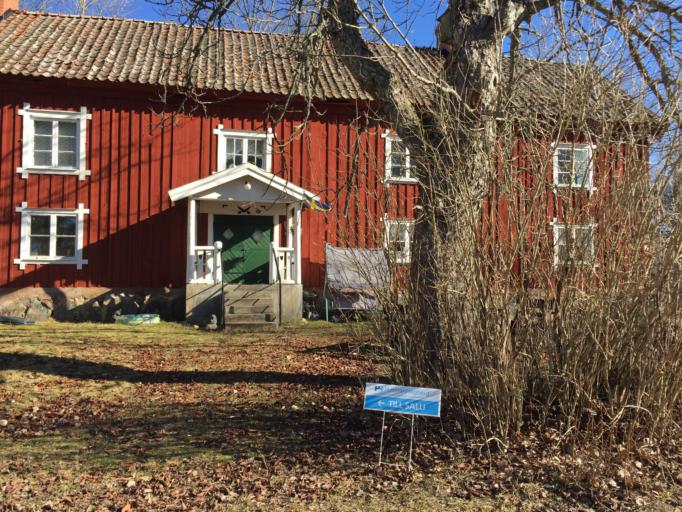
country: SE
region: OErebro
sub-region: Orebro Kommun
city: Odensbacken
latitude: 59.0296
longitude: 15.6623
